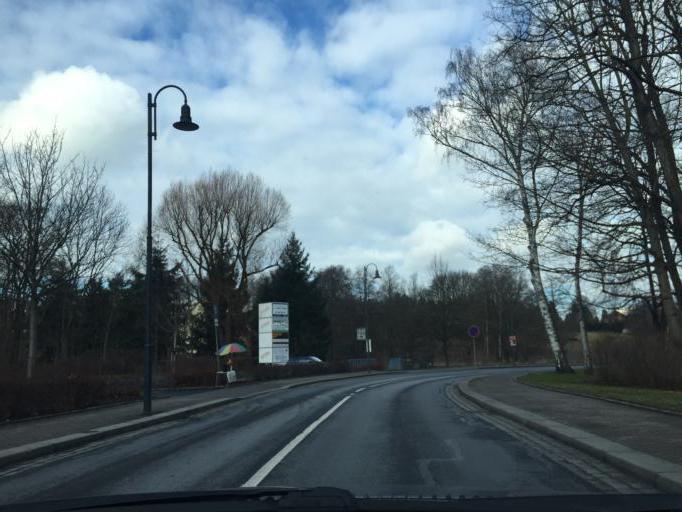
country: DE
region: Saxony
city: Radeberg
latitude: 51.1166
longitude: 13.9164
